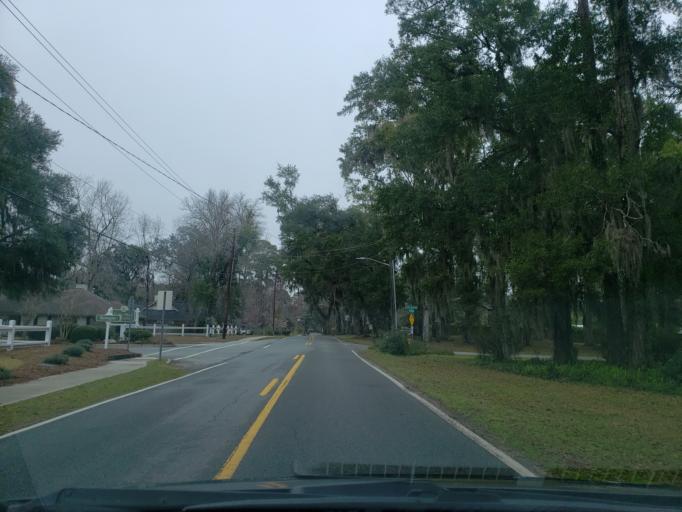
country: US
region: Georgia
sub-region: Chatham County
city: Montgomery
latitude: 31.9394
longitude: -81.1514
